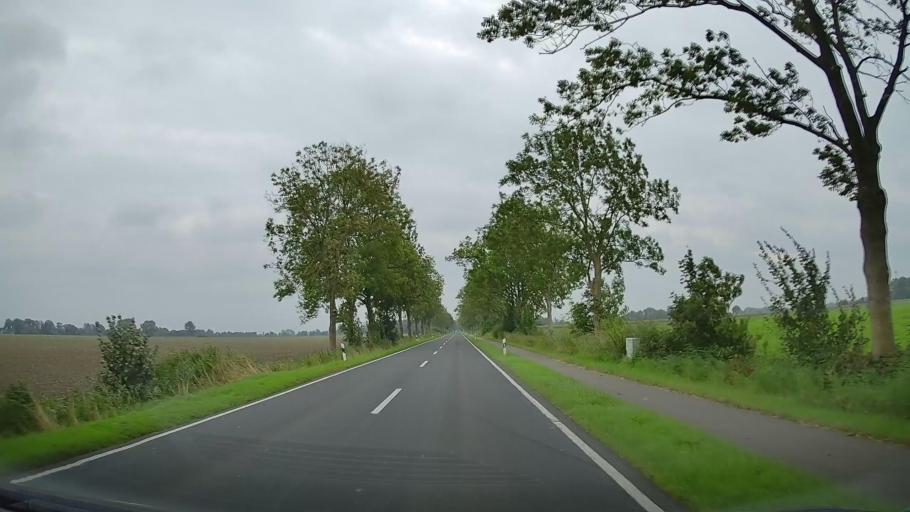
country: DE
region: Lower Saxony
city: Freiburg
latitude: 53.8178
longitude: 9.2958
